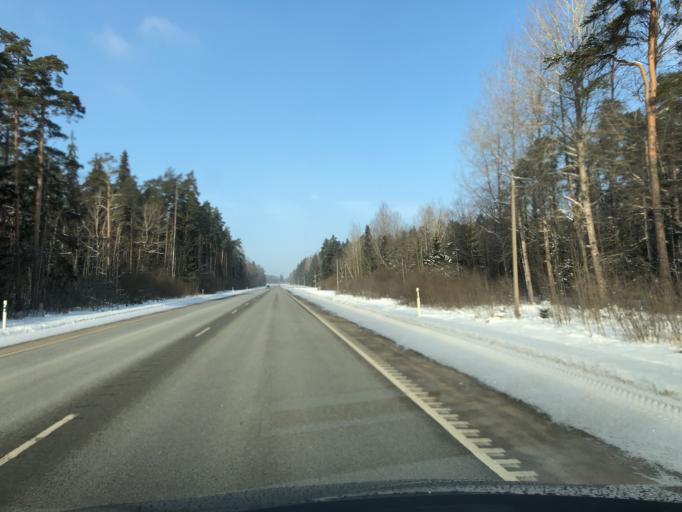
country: EE
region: Tartu
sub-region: Tartu linn
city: Tartu
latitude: 58.3978
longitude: 26.6600
